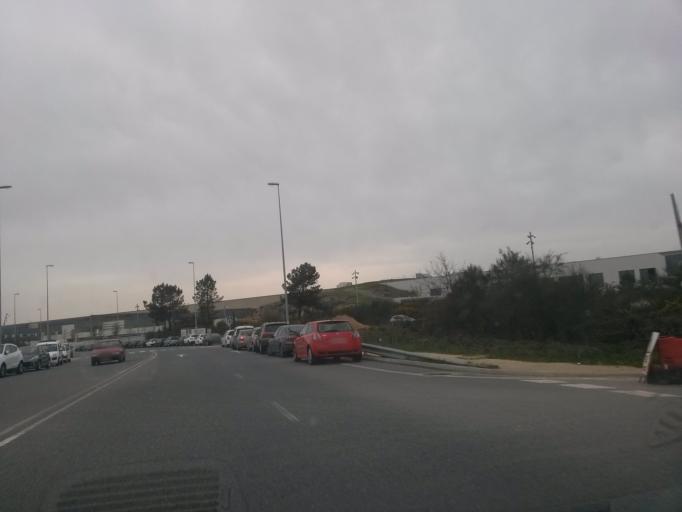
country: ES
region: Galicia
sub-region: Provincia de Lugo
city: Lugo
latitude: 43.0205
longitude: -7.5299
